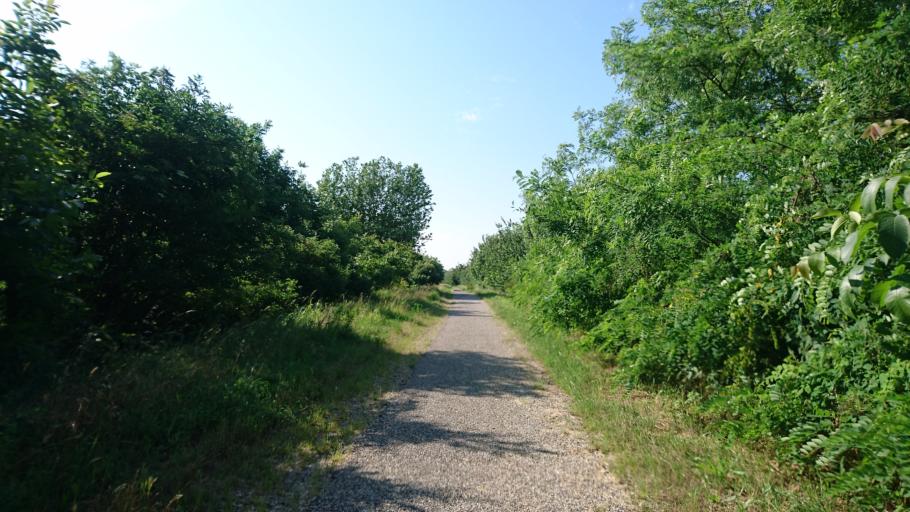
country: IT
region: Veneto
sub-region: Provincia di Verona
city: Villa Bartolomea
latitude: 45.1778
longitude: 11.3308
